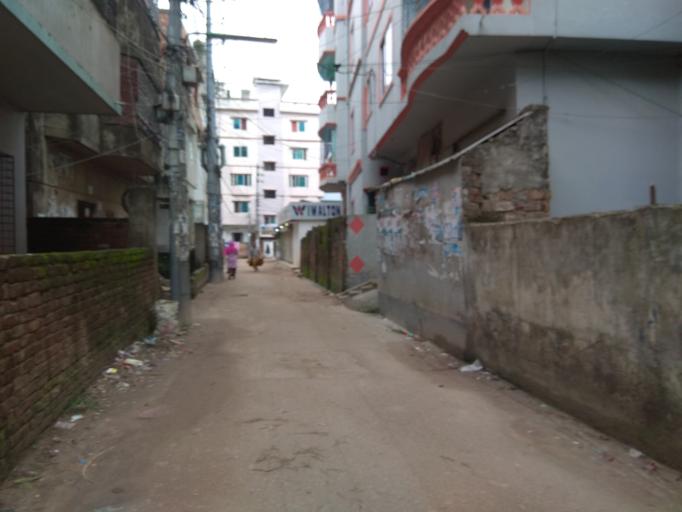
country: BD
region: Dhaka
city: Azimpur
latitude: 23.7967
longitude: 90.3687
